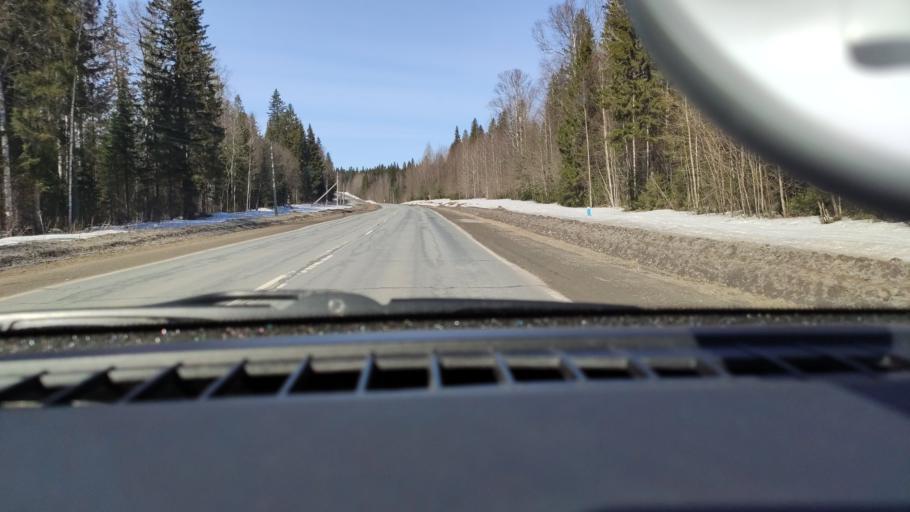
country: RU
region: Perm
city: Perm
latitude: 58.1995
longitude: 56.2066
